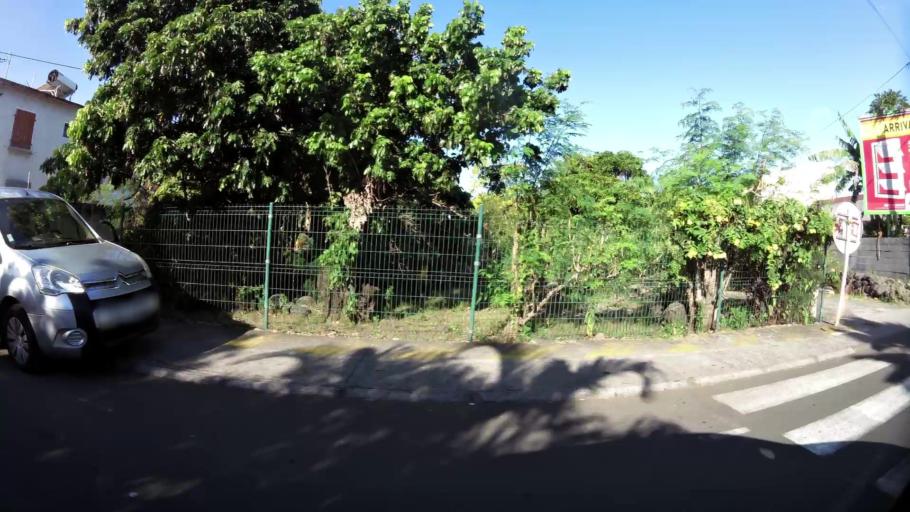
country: RE
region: Reunion
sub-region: Reunion
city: Saint-Louis
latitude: -21.2909
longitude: 55.4099
